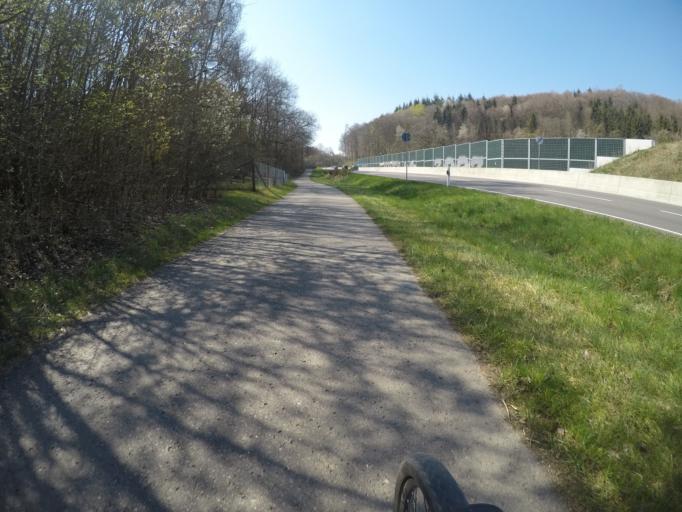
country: DE
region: Baden-Wuerttemberg
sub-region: Regierungsbezirk Stuttgart
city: Renningen
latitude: 48.7575
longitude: 8.9266
